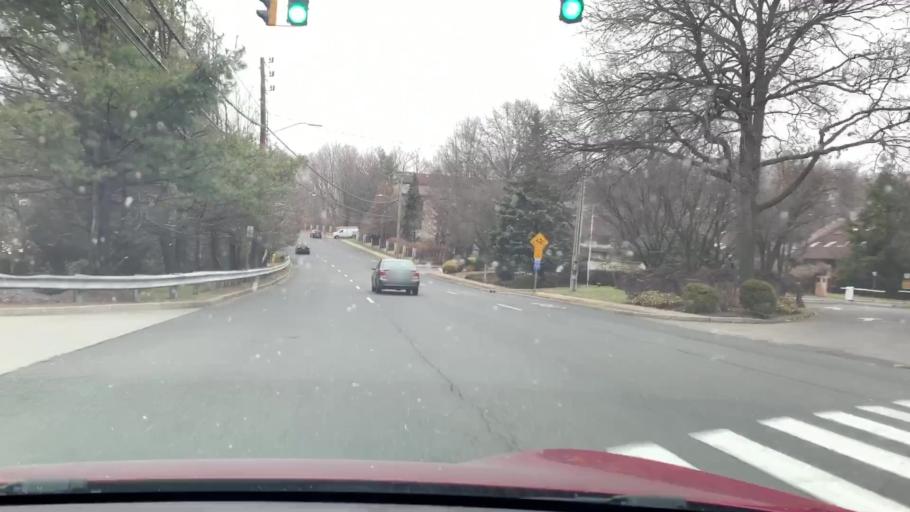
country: US
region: Connecticut
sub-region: Fairfield County
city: Stamford
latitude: 41.0689
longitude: -73.5449
